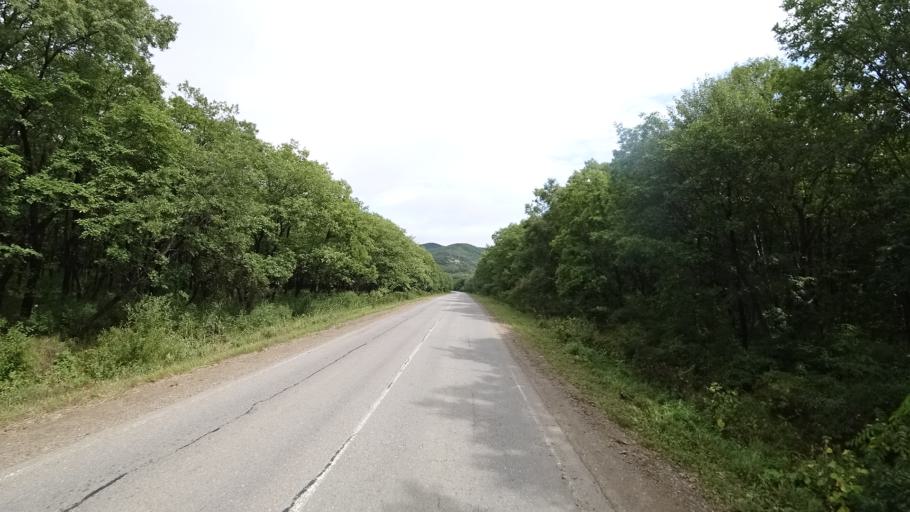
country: RU
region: Primorskiy
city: Lyalichi
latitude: 44.1396
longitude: 132.4217
